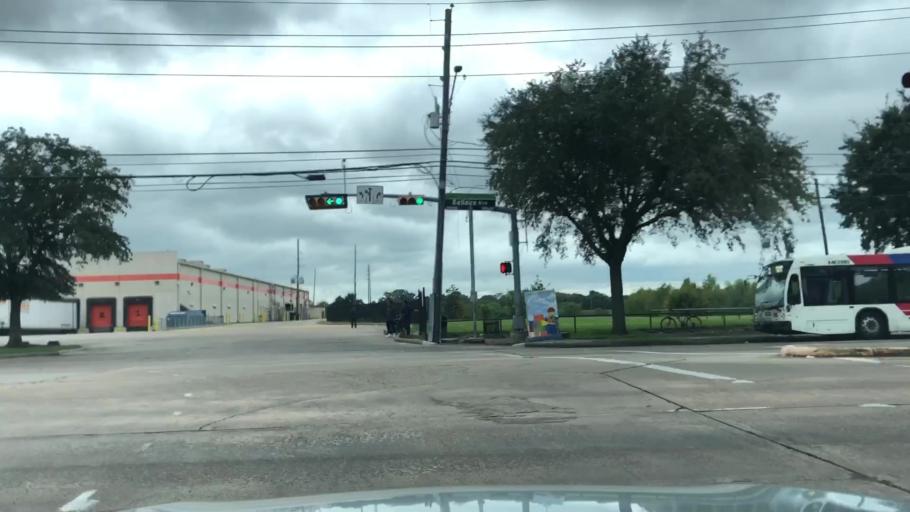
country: US
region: Texas
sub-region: Fort Bend County
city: Meadows Place
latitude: 29.7045
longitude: -95.5603
